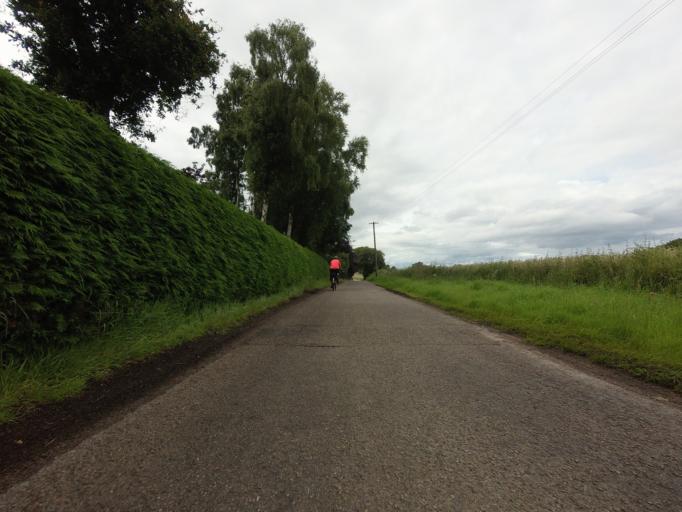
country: GB
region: Scotland
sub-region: Moray
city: Forres
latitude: 57.6040
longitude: -3.7468
